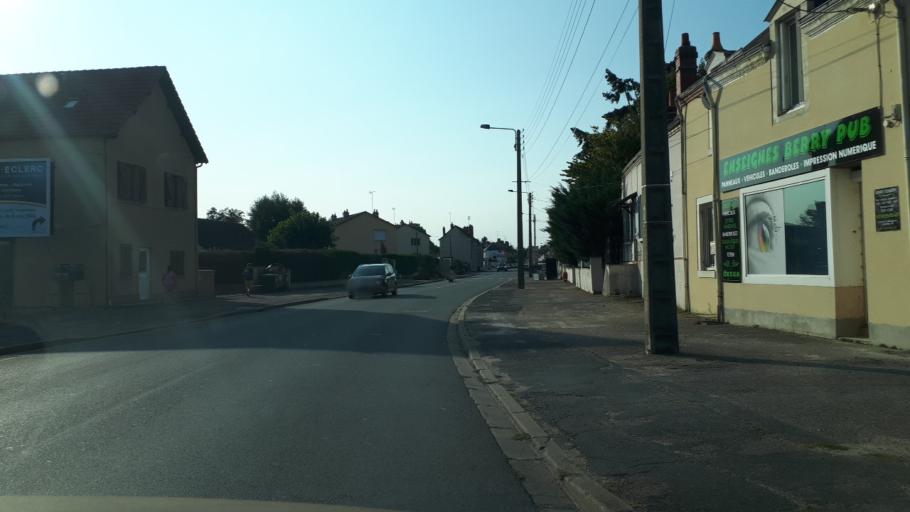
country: FR
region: Centre
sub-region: Departement du Cher
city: Vierzon
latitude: 47.2156
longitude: 2.1059
